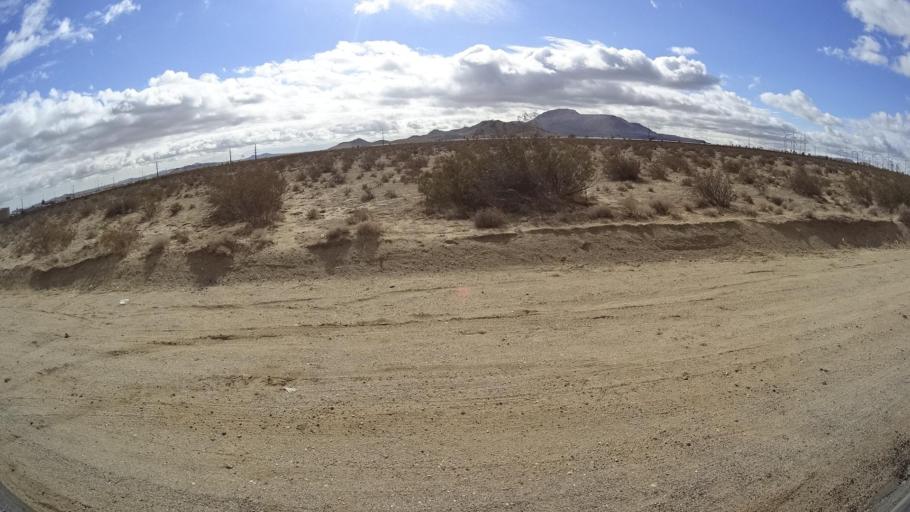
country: US
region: California
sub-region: Kern County
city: Mojave
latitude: 35.0319
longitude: -118.1717
